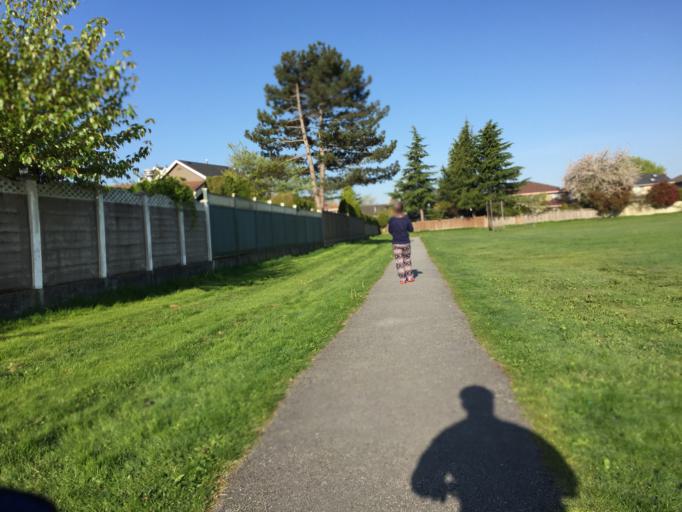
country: CA
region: British Columbia
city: Richmond
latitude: 49.1531
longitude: -123.1443
